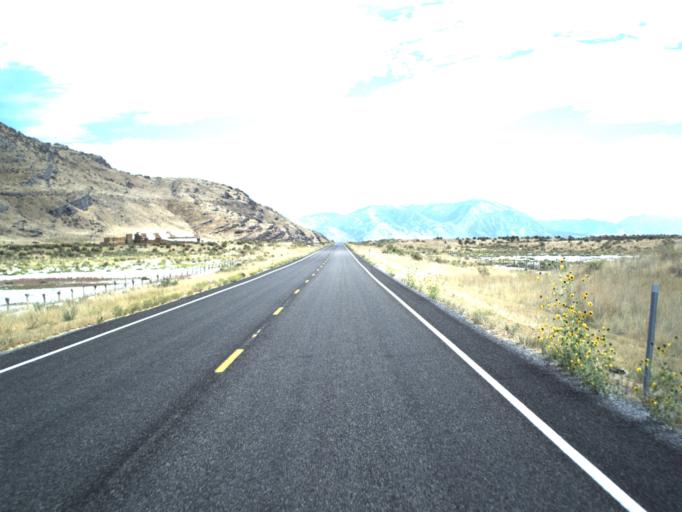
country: US
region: Utah
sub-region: Box Elder County
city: Tremonton
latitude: 41.5868
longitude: -112.2666
